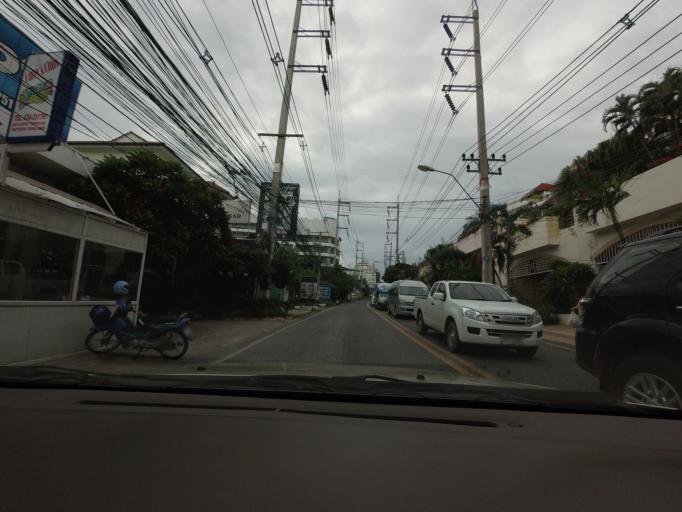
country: TH
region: Chon Buri
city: Phatthaya
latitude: 12.9131
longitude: 100.8674
